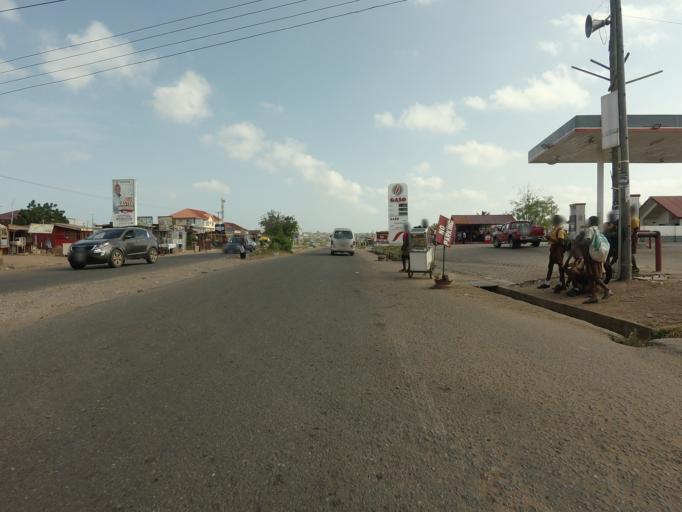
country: GH
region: Greater Accra
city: Tema
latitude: 5.6601
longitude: -0.0517
